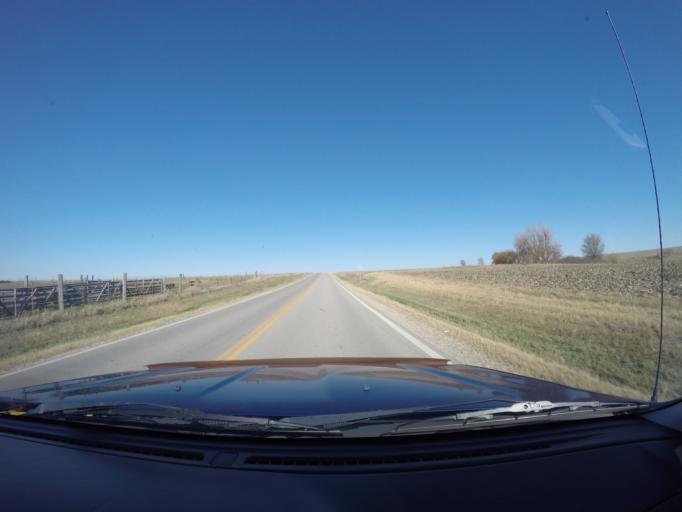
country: US
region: Kansas
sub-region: Marshall County
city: Marysville
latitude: 39.8484
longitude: -96.4170
